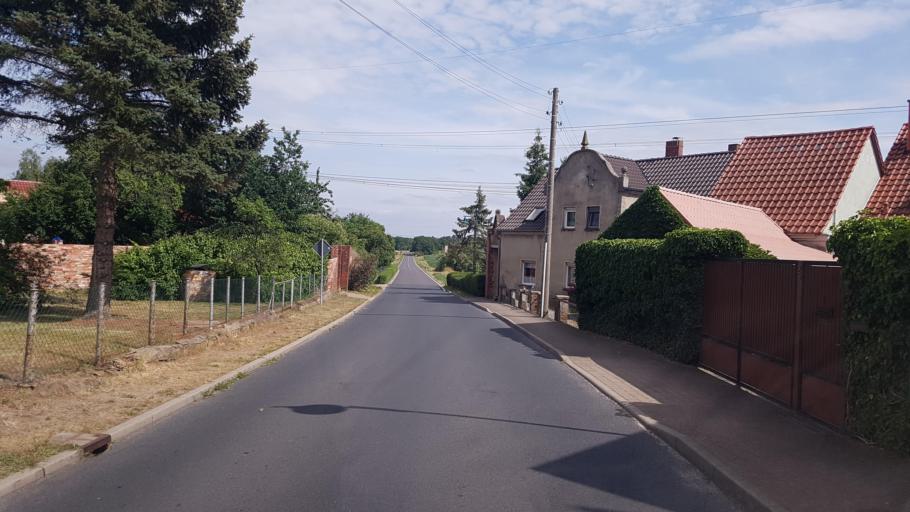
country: DE
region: Saxony-Anhalt
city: Abtsdorf
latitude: 51.9000
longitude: 12.7050
